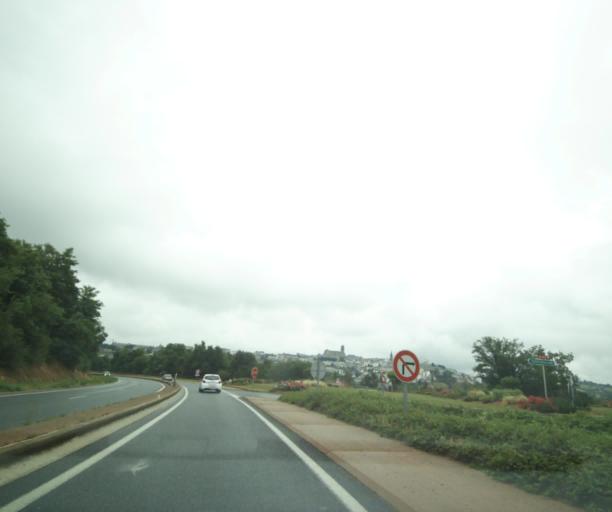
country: FR
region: Midi-Pyrenees
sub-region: Departement de l'Aveyron
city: Olemps
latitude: 44.3388
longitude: 2.5614
